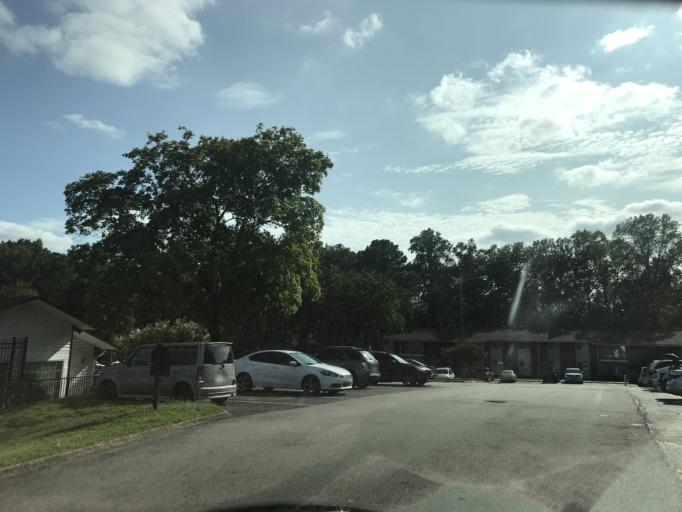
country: US
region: North Carolina
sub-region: Wake County
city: Raleigh
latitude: 35.8378
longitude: -78.5990
